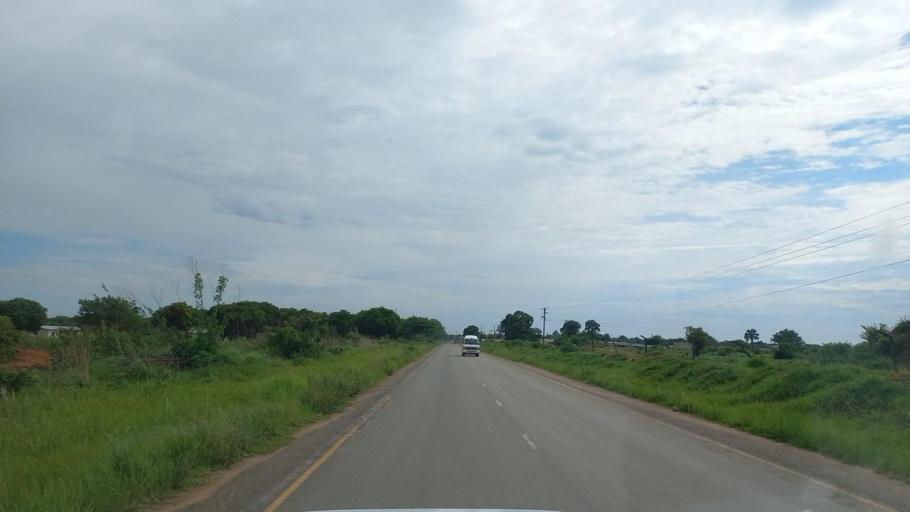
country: ZM
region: Copperbelt
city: Kitwe
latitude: -12.8812
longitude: 28.3210
